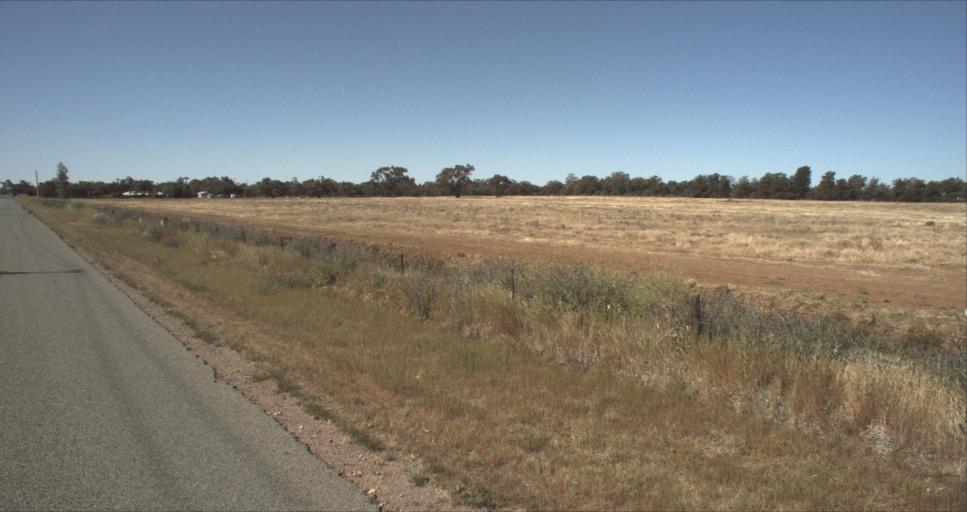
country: AU
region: New South Wales
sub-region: Leeton
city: Leeton
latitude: -34.5636
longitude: 146.3831
